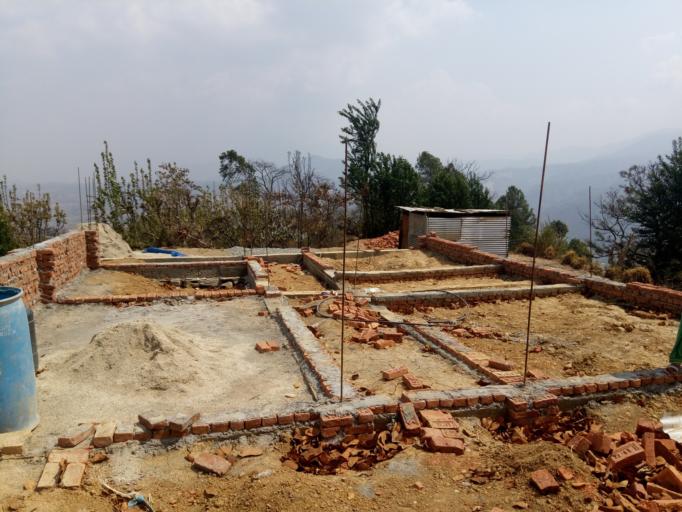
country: NP
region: Central Region
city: Kirtipur
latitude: 27.5954
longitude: 85.2651
